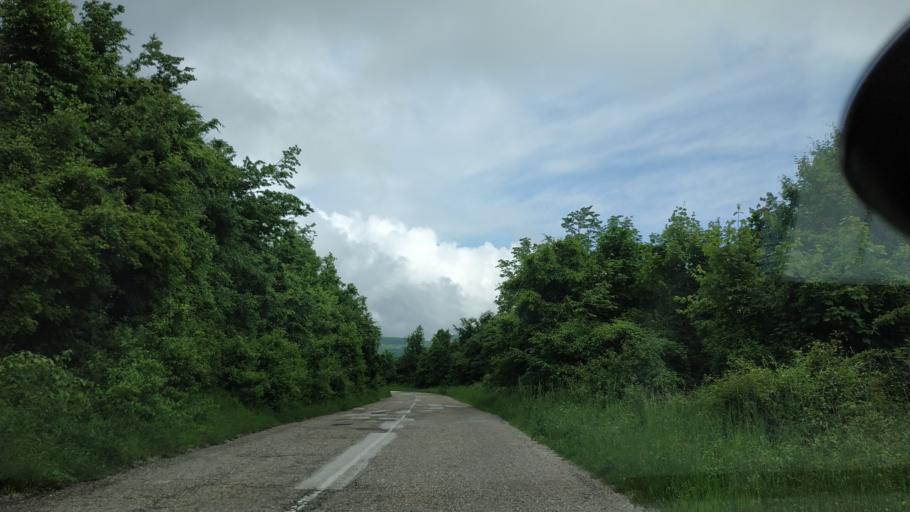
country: RS
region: Central Serbia
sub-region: Zajecarski Okrug
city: Boljevac
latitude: 43.7242
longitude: 21.9529
